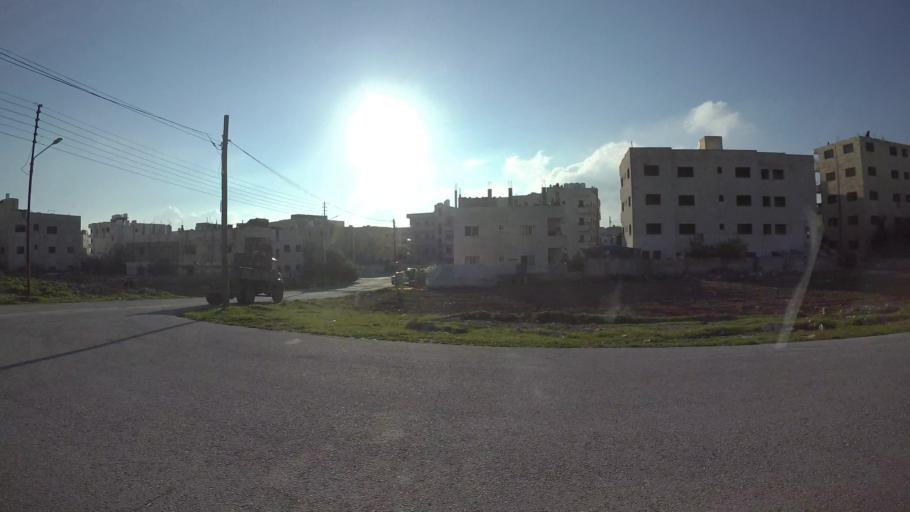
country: JO
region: Amman
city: Al Bunayyat ash Shamaliyah
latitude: 31.9003
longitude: 35.9079
